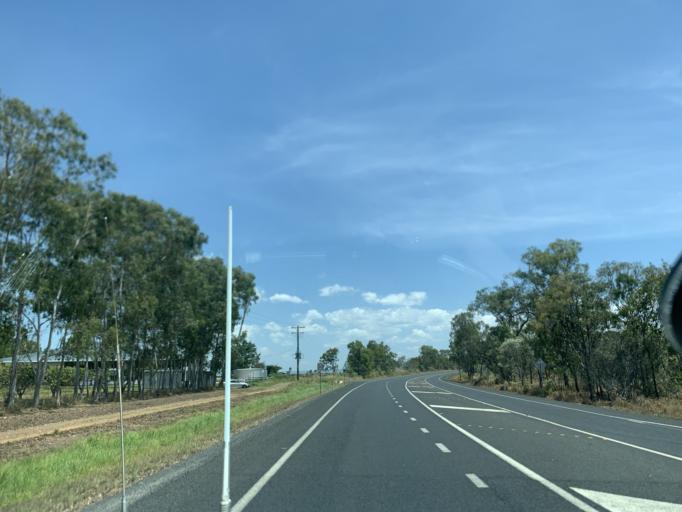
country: AU
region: Queensland
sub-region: Tablelands
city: Mareeba
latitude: -16.9794
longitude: 145.5317
